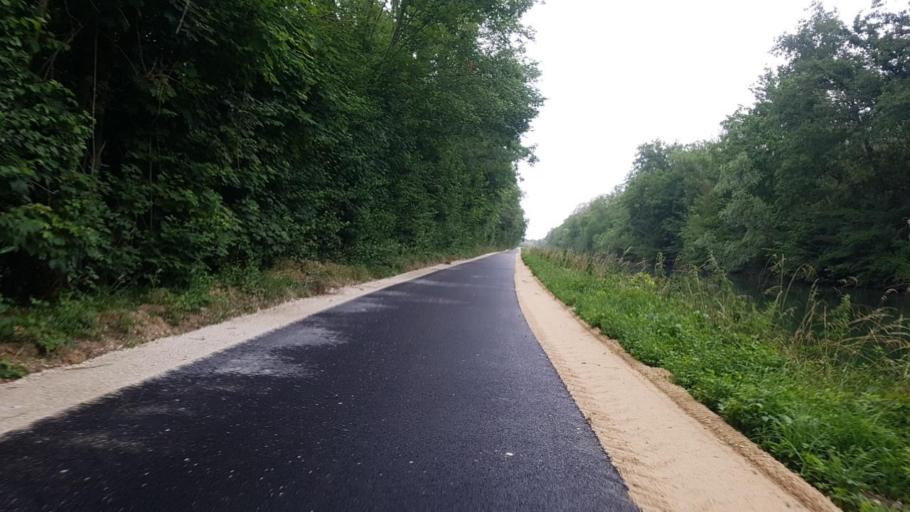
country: FR
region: Champagne-Ardenne
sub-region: Departement de la Marne
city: Vitry-le-Francois
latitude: 48.8010
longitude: 4.5236
